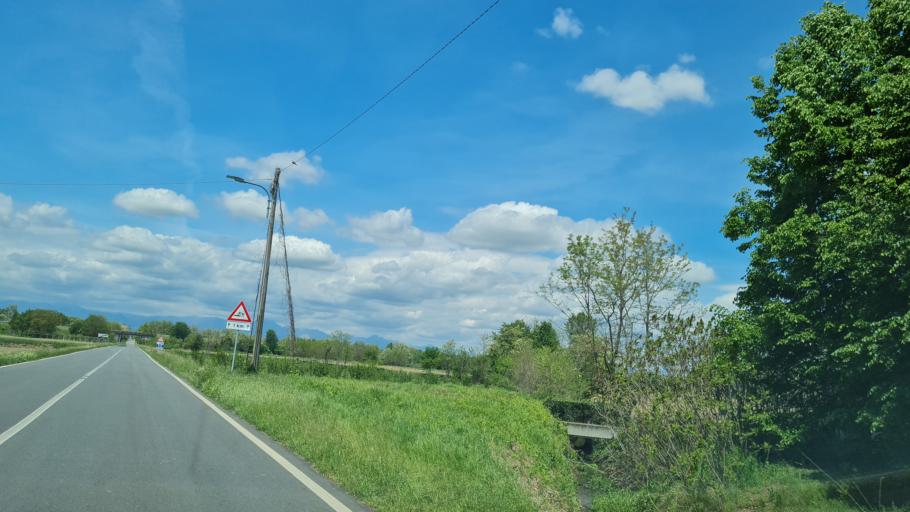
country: IT
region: Piedmont
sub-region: Provincia di Novara
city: Sillavengo
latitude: 45.5235
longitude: 8.4370
